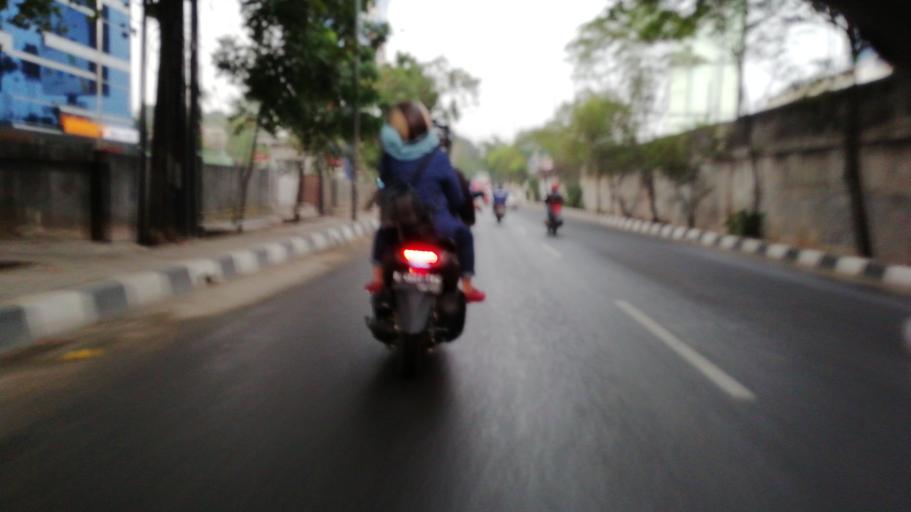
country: ID
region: Jakarta Raya
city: Jakarta
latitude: -6.3000
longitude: 106.8343
